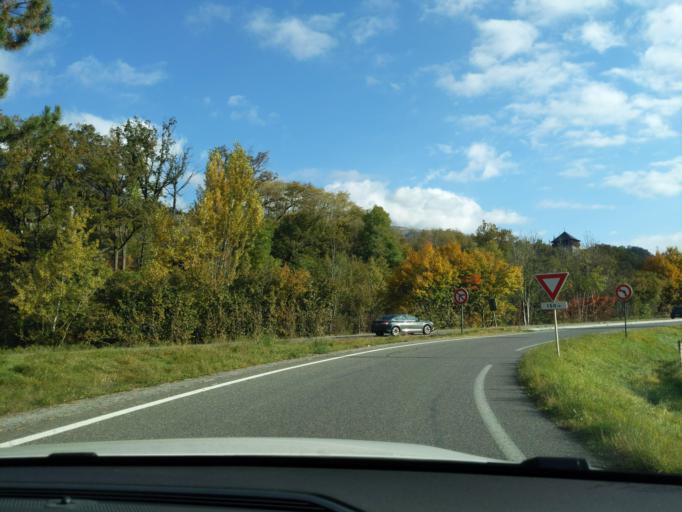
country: FR
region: Rhone-Alpes
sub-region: Departement de la Savoie
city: Aime
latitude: 45.5530
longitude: 6.6489
